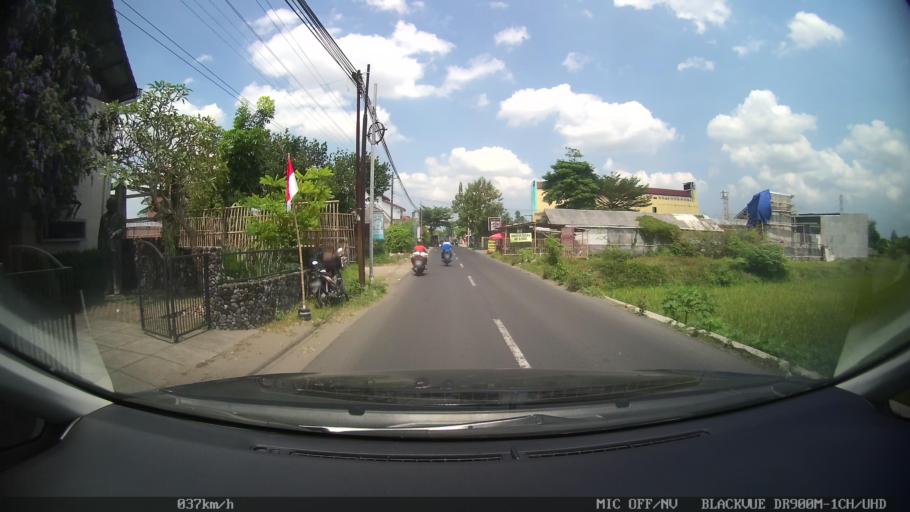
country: ID
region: Daerah Istimewa Yogyakarta
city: Kasihan
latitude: -7.8207
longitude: 110.3478
